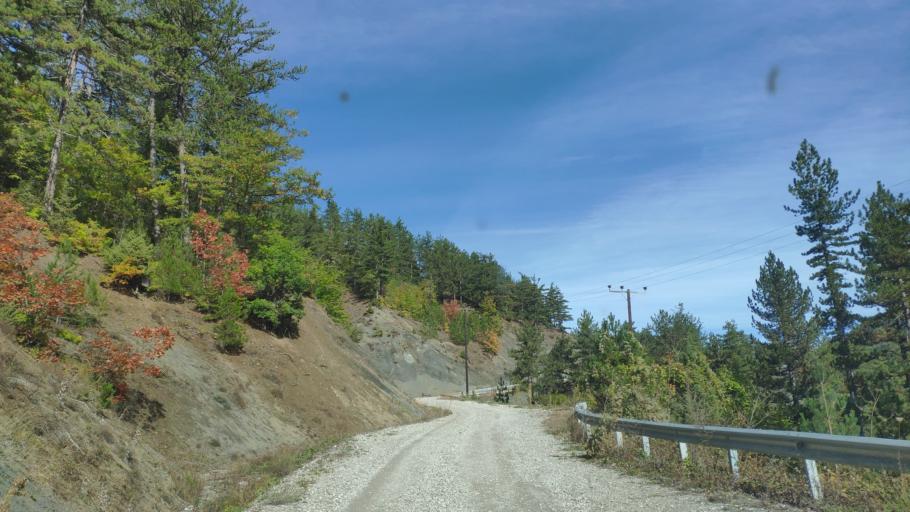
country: AL
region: Korce
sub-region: Rrethi i Devollit
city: Miras
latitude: 40.4168
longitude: 20.8702
